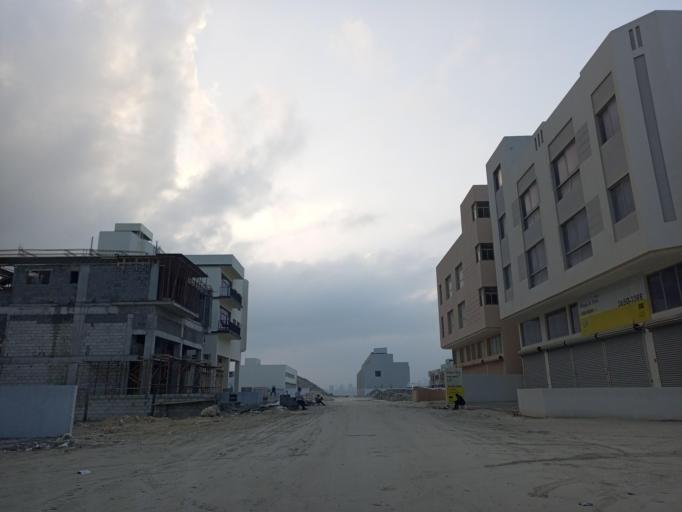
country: BH
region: Muharraq
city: Al Hadd
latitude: 26.2353
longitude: 50.6451
